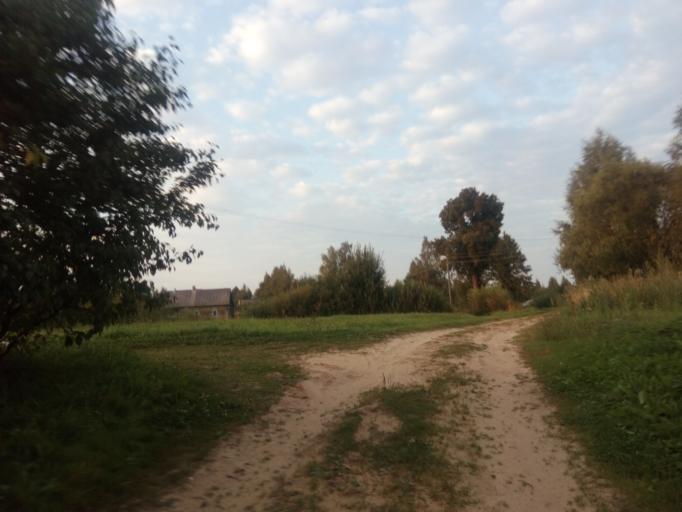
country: BY
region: Vitebsk
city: Dzisna
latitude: 55.6561
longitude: 28.3291
